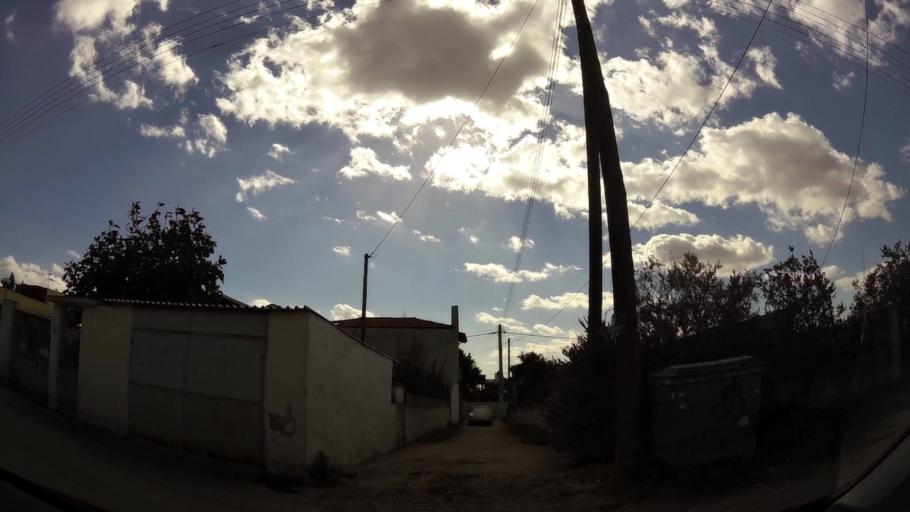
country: GR
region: Attica
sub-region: Nomarchia Anatolikis Attikis
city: Thrakomakedones
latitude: 38.1065
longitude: 23.7467
